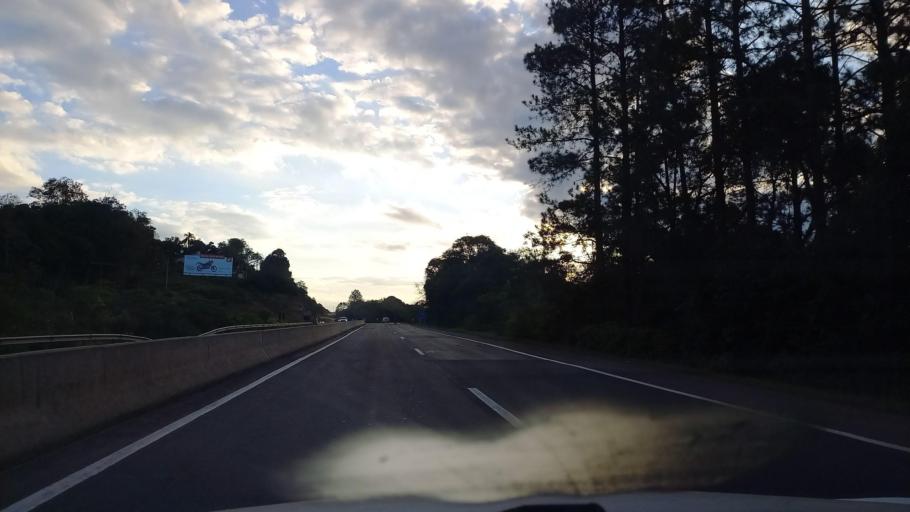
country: BR
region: Rio Grande do Sul
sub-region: Santa Cruz Do Sul
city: Santa Cruz do Sul
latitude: -29.6918
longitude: -52.3881
